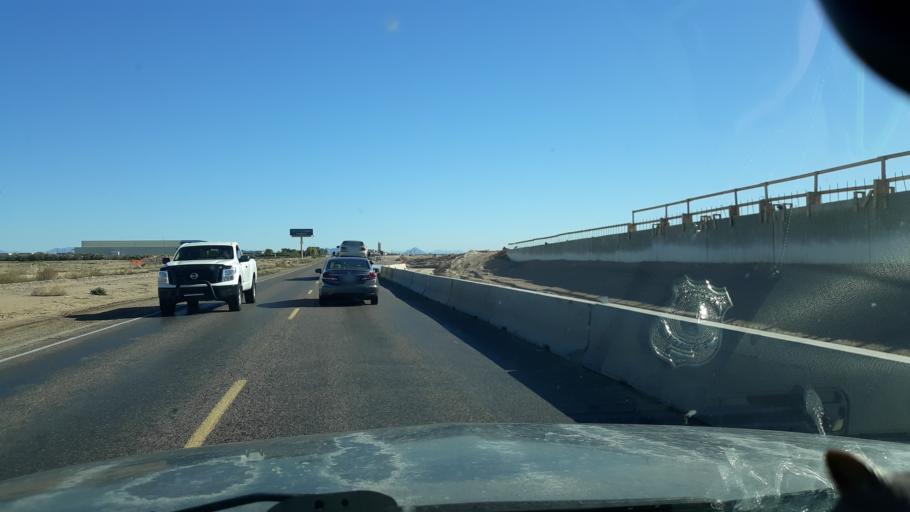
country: US
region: Arizona
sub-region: Maricopa County
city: Youngtown
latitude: 33.5511
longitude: -112.3387
